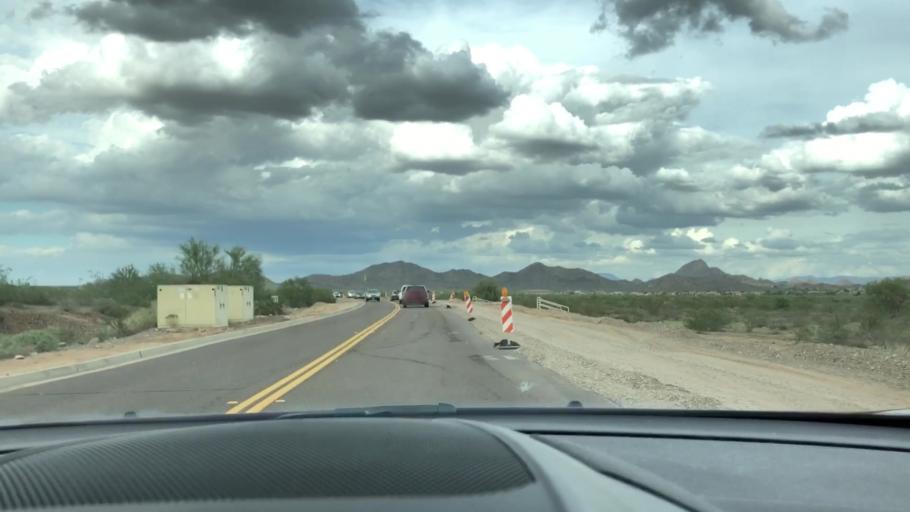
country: US
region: Arizona
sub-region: Maricopa County
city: Sun City West
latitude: 33.7113
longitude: -112.2343
